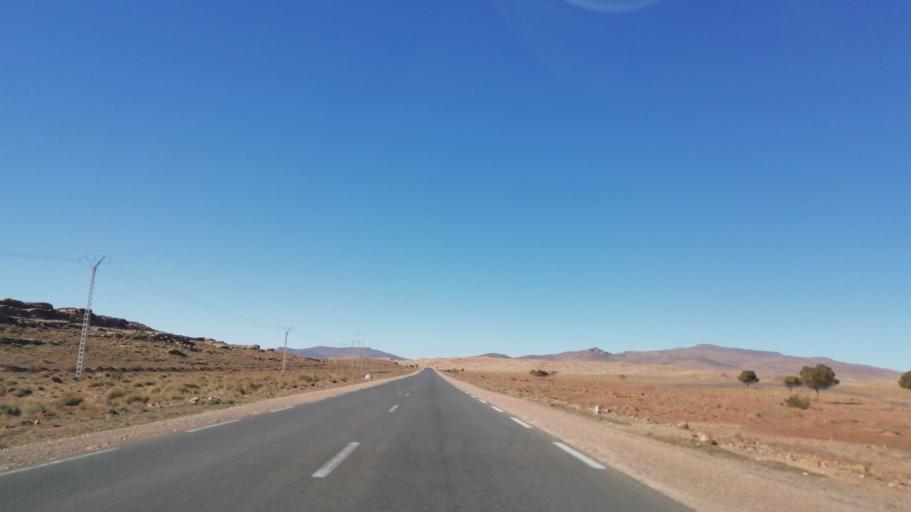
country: DZ
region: El Bayadh
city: El Bayadh
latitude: 33.6162
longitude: 1.2087
